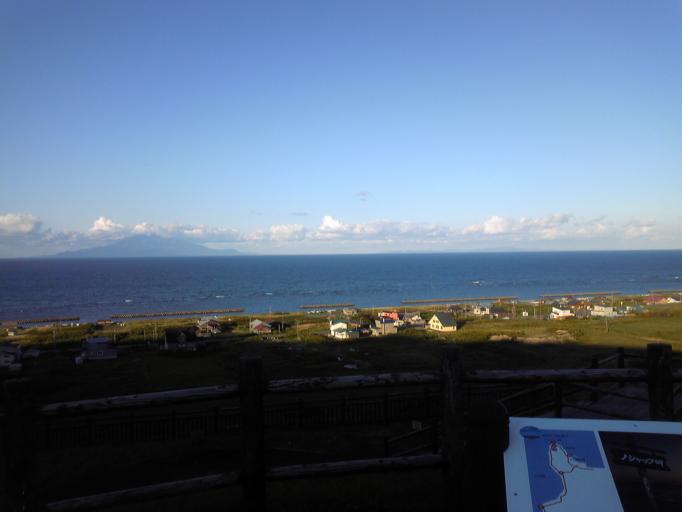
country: JP
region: Hokkaido
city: Wakkanai
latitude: 45.3800
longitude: 141.6536
